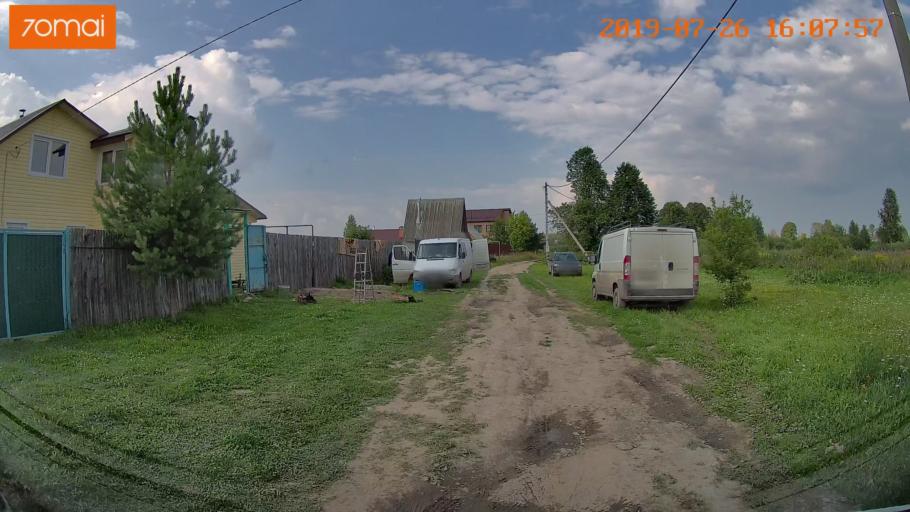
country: RU
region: Ivanovo
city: Bogorodskoye
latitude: 57.0613
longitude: 41.0572
